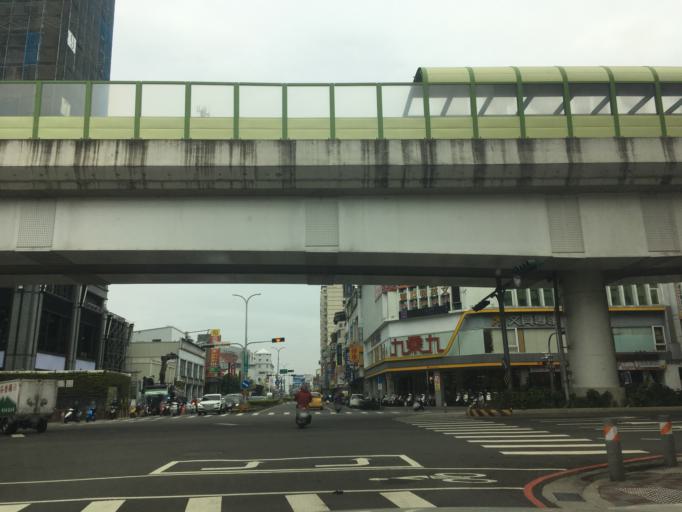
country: TW
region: Taiwan
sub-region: Taichung City
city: Taichung
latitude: 24.1714
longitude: 120.6612
